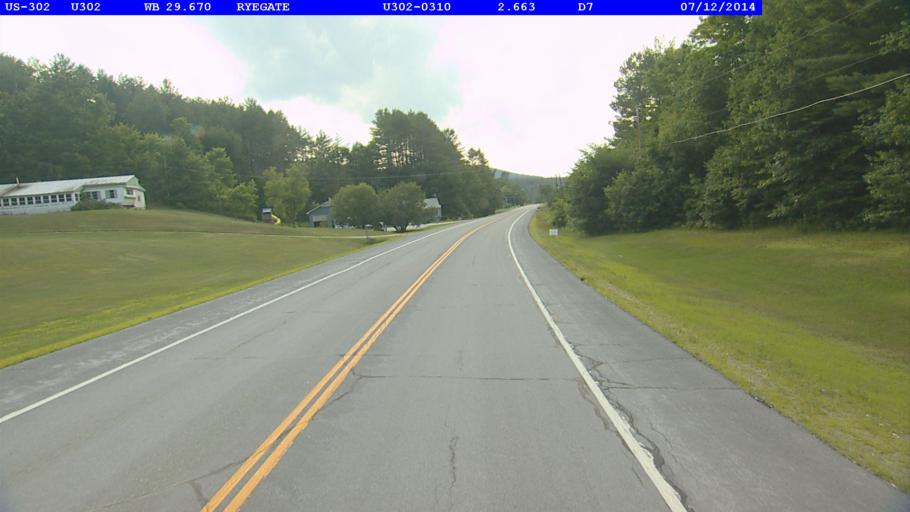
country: US
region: New Hampshire
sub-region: Grafton County
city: Woodsville
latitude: 44.1845
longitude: -72.1298
